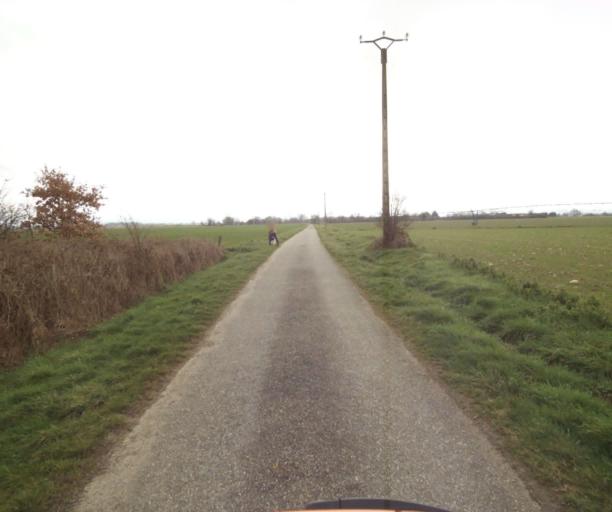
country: FR
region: Midi-Pyrenees
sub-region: Departement de l'Ariege
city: La Tour-du-Crieu
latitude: 43.1672
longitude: 1.6852
